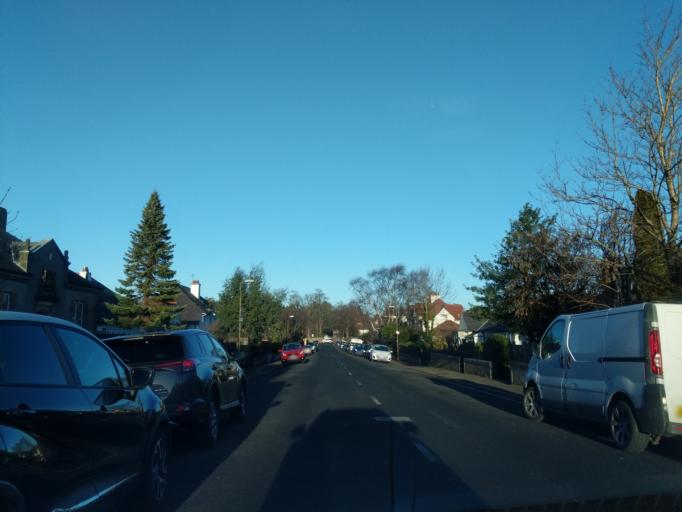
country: GB
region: Scotland
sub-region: Edinburgh
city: Colinton
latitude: 55.9066
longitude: -3.2508
